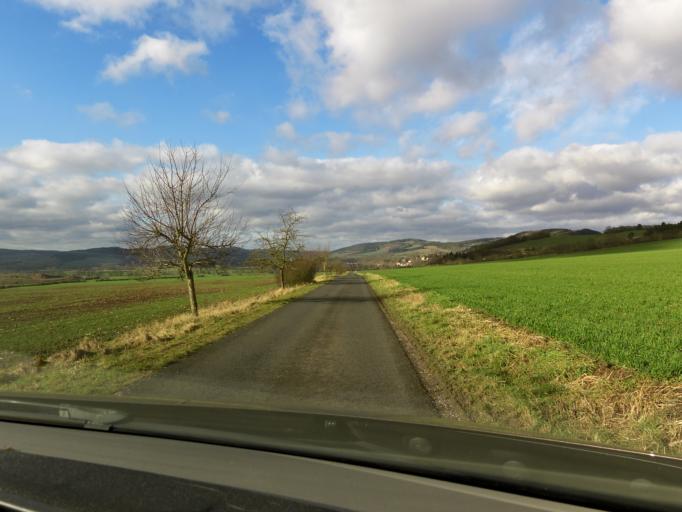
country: DE
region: Thuringia
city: Creuzburg
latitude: 51.0412
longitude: 10.2678
